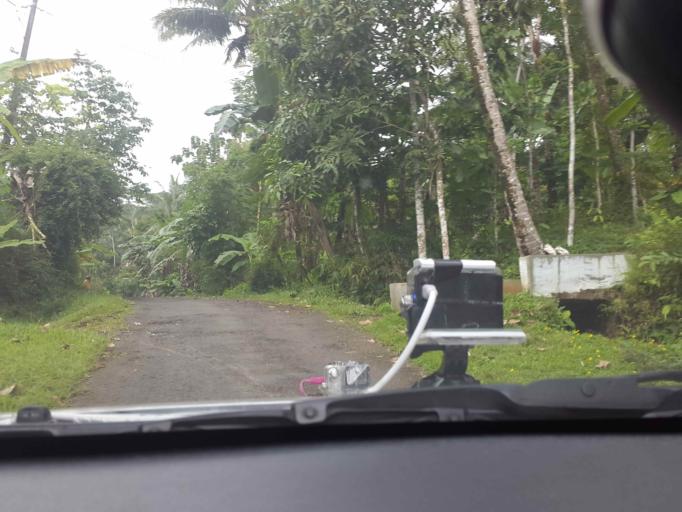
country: ID
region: Central Java
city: Banyumas
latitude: -7.5633
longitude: 109.3472
